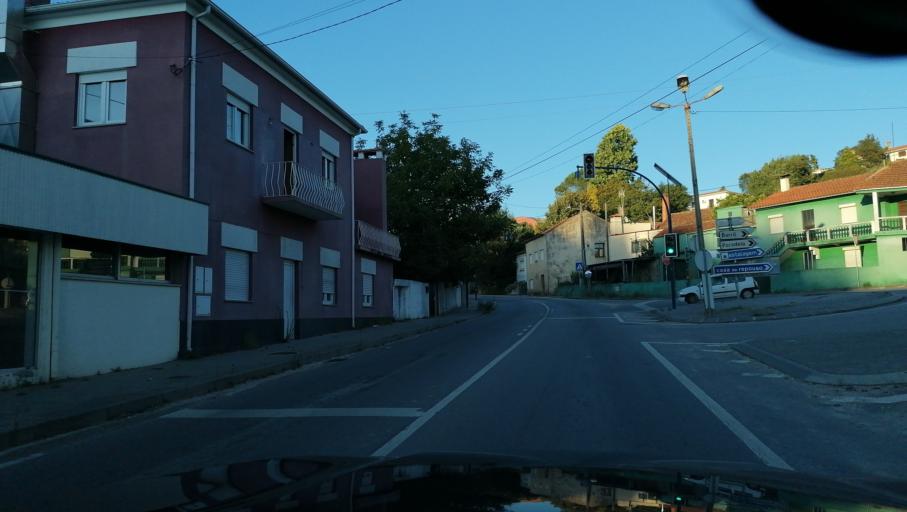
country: PT
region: Aveiro
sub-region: Oliveira do Bairro
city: Oliveira do Bairro
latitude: 40.5573
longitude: -8.4889
